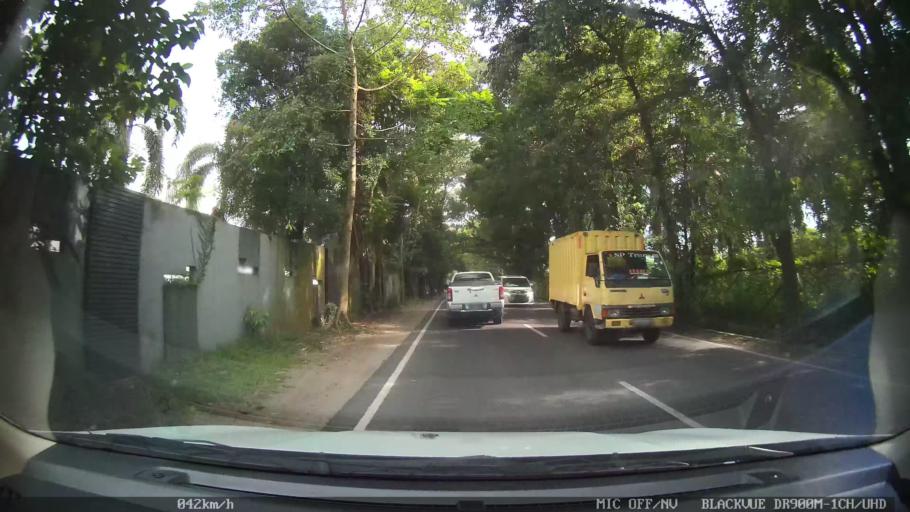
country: ID
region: North Sumatra
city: Medan
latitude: 3.5665
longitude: 98.6836
